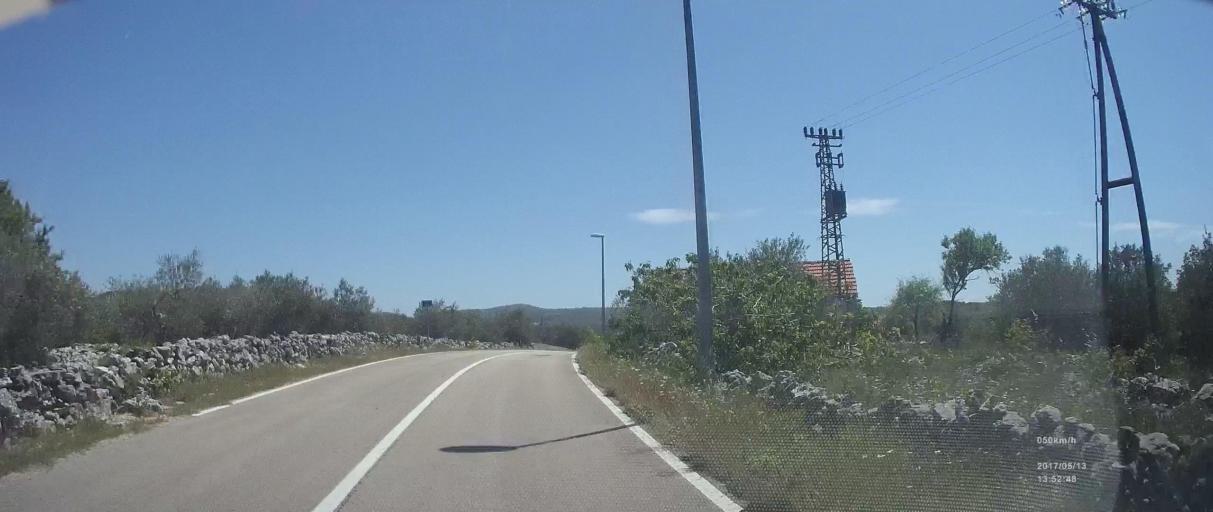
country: HR
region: Sibensko-Kniniska
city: Primosten
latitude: 43.6039
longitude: 15.9966
